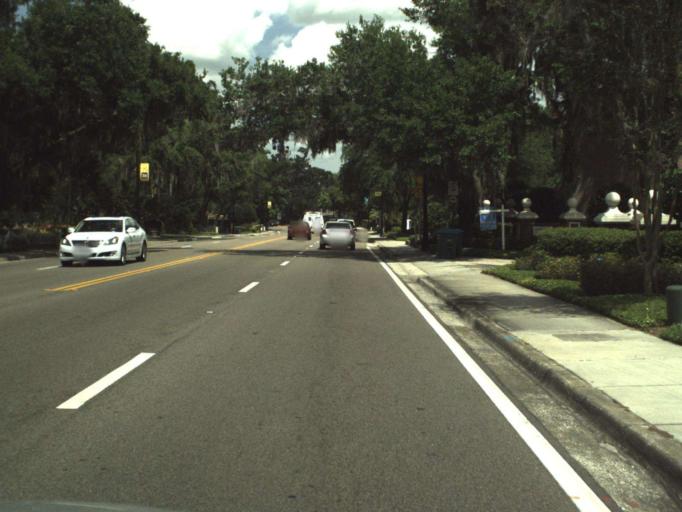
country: US
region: Florida
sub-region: Orange County
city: Winter Park
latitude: 28.5956
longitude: -81.3444
